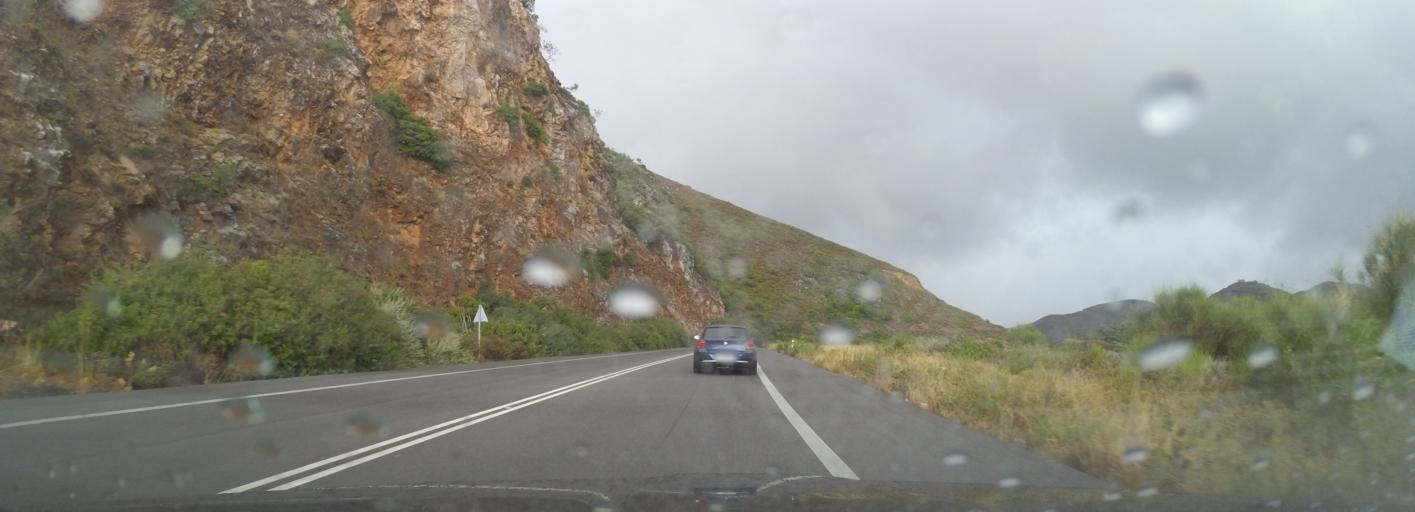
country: GR
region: Crete
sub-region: Nomos Rethymnis
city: Anogeia
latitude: 35.3906
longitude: 24.9029
